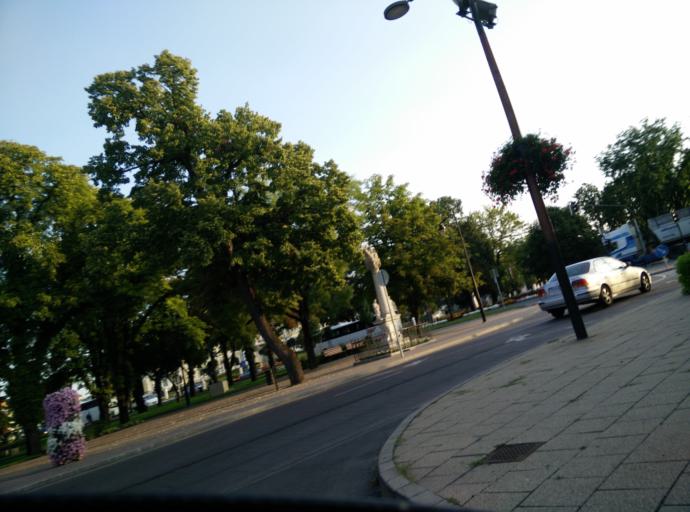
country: HU
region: Heves
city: Hatvan
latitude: 47.6665
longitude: 19.6839
